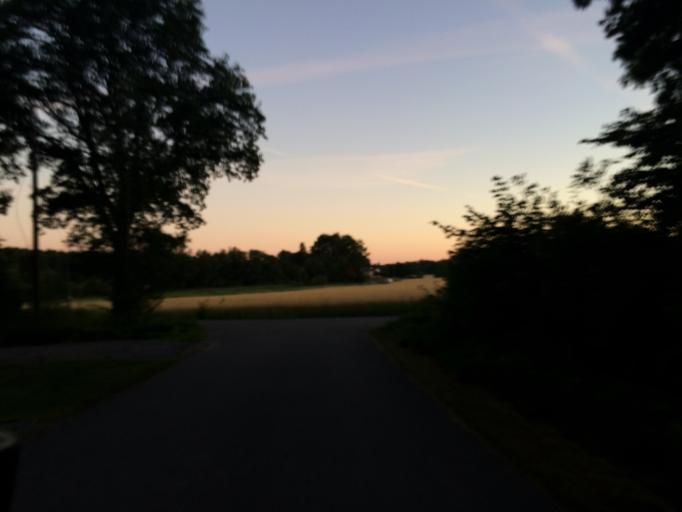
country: SE
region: Soedermanland
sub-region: Eskilstuna Kommun
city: Kvicksund
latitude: 59.4452
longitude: 16.3102
